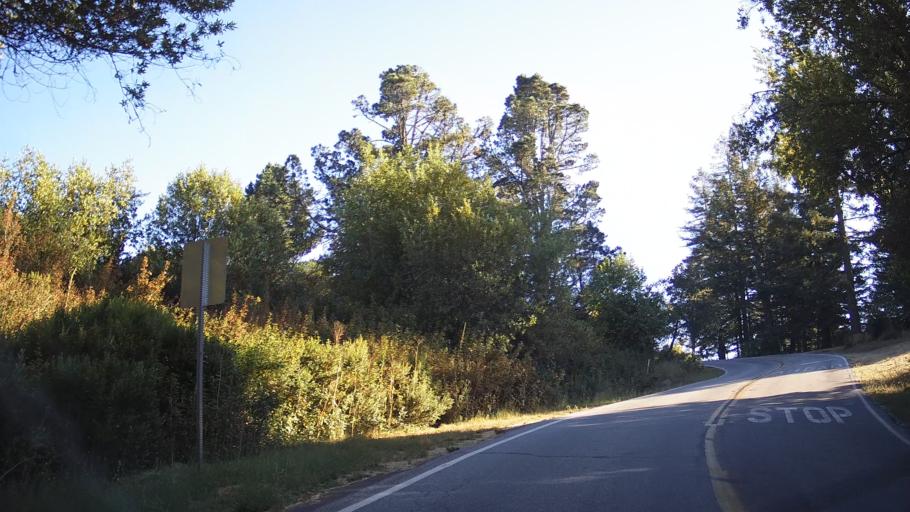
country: US
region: California
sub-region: Contra Costa County
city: Orinda
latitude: 37.8805
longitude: -122.2256
